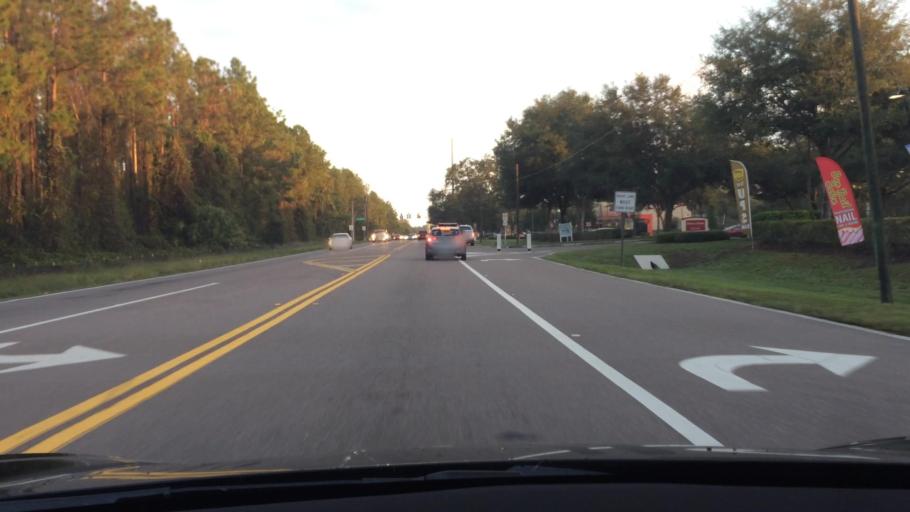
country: US
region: Florida
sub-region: Hillsborough County
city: Citrus Park
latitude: 28.1272
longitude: -82.5750
